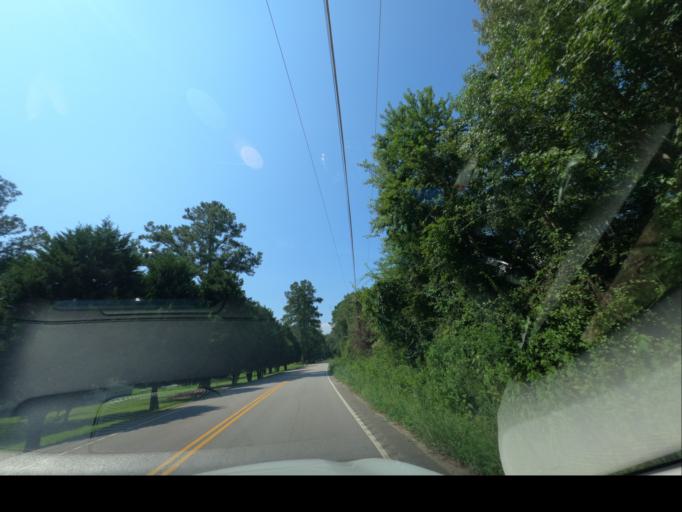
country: US
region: South Carolina
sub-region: Richland County
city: Hopkins
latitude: 33.8512
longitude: -80.8744
